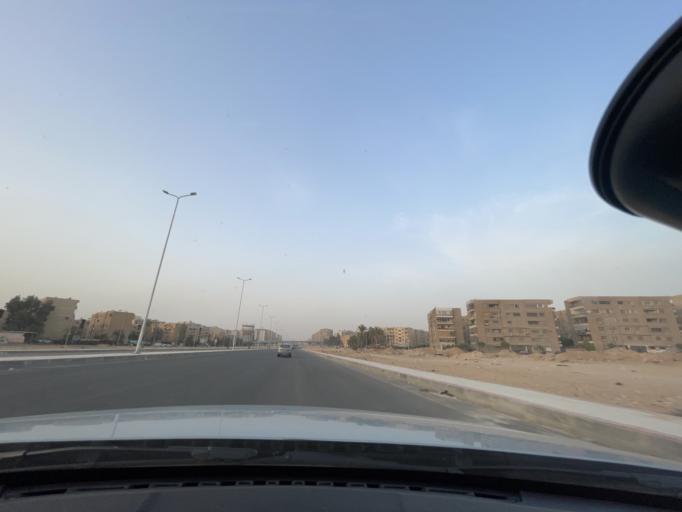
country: EG
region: Muhafazat al Qahirah
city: Cairo
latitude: 30.0427
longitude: 31.3614
